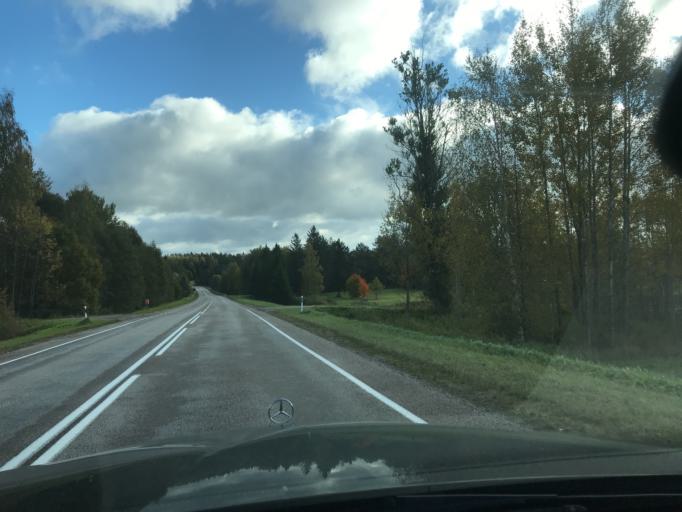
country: EE
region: Valgamaa
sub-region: Torva linn
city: Torva
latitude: 57.9857
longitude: 26.0406
